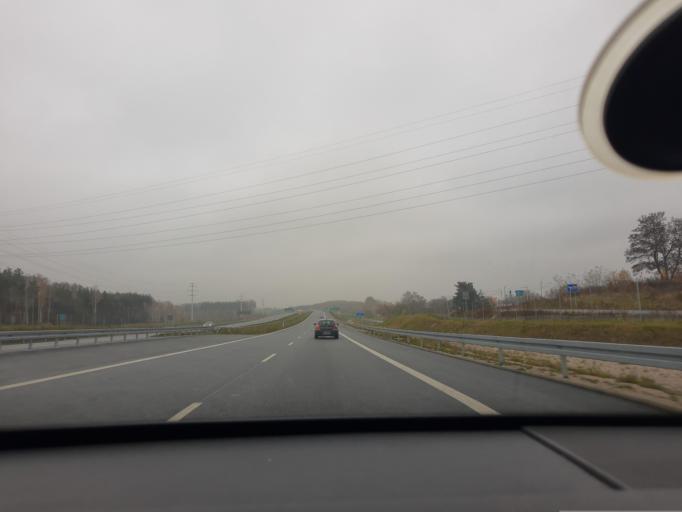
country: PL
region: Lodz Voivodeship
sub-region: Powiat pabianicki
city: Konstantynow Lodzki
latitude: 51.7121
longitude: 19.3468
